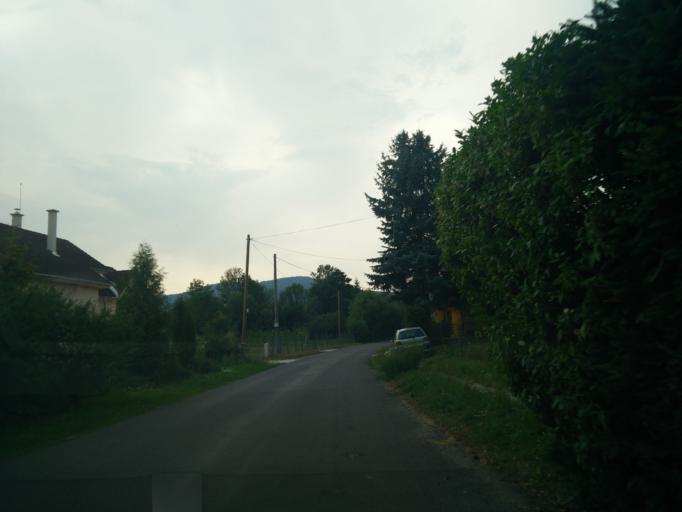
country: SK
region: Nitriansky
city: Handlova
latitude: 48.6504
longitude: 18.7880
